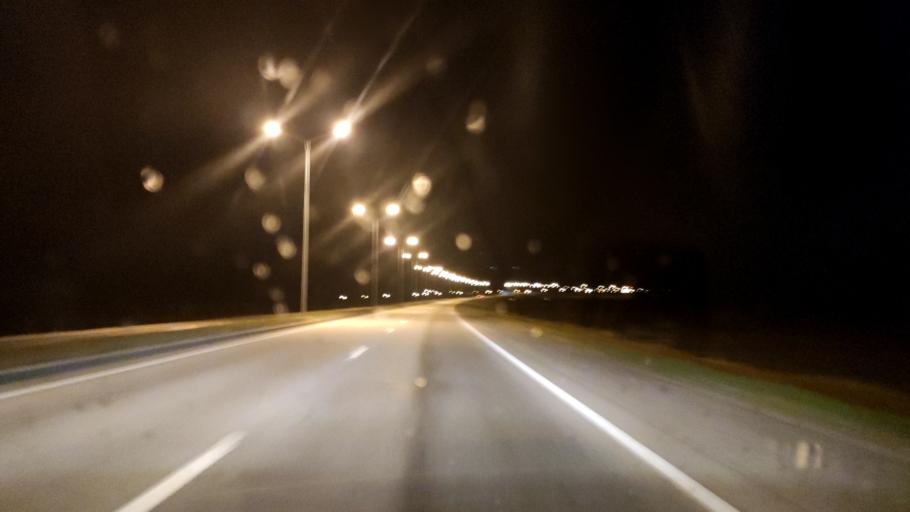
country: RU
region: Belgorod
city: Staryy Oskol
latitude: 51.3184
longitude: 37.7453
